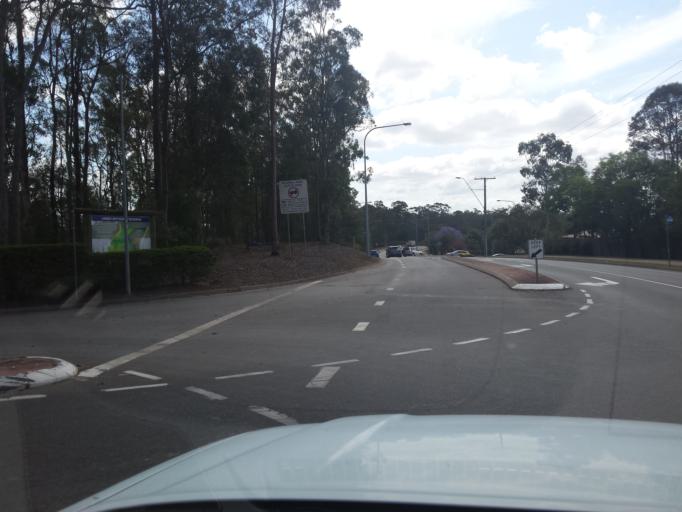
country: AU
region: Queensland
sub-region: Moreton Bay
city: Ferny Hills
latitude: -27.3830
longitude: 152.9414
